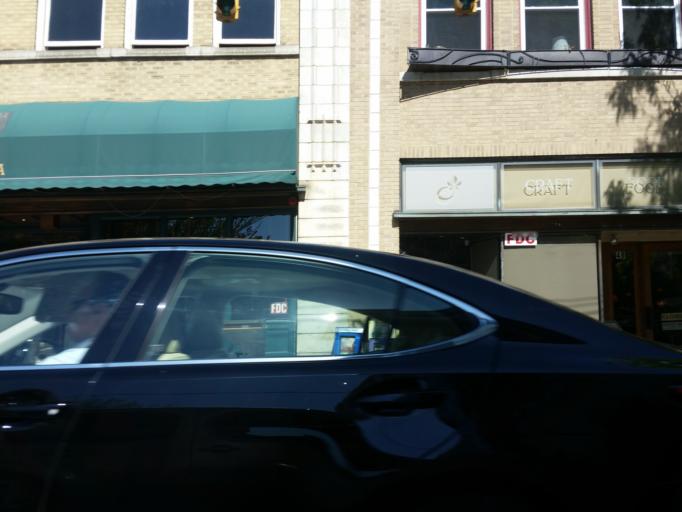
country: US
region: North Carolina
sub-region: Buncombe County
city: Asheville
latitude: 35.5932
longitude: -82.5512
